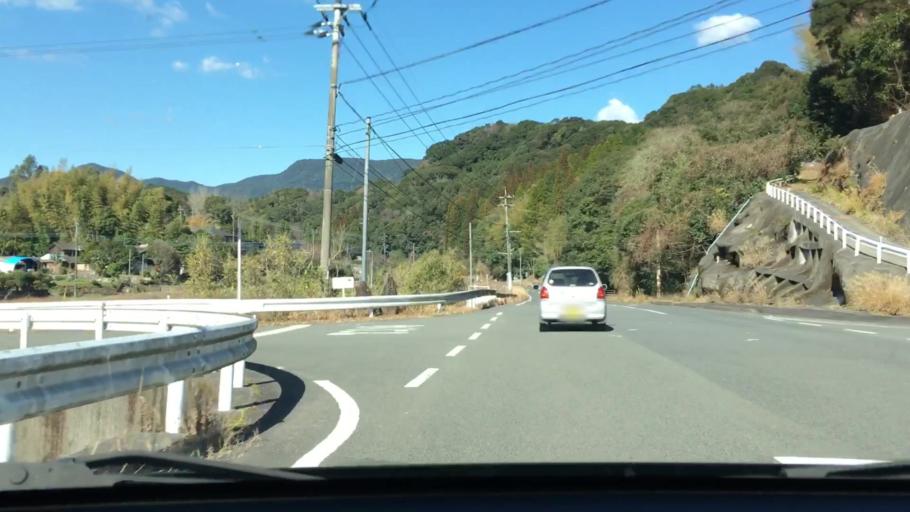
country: JP
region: Kagoshima
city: Ijuin
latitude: 31.6946
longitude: 130.4617
